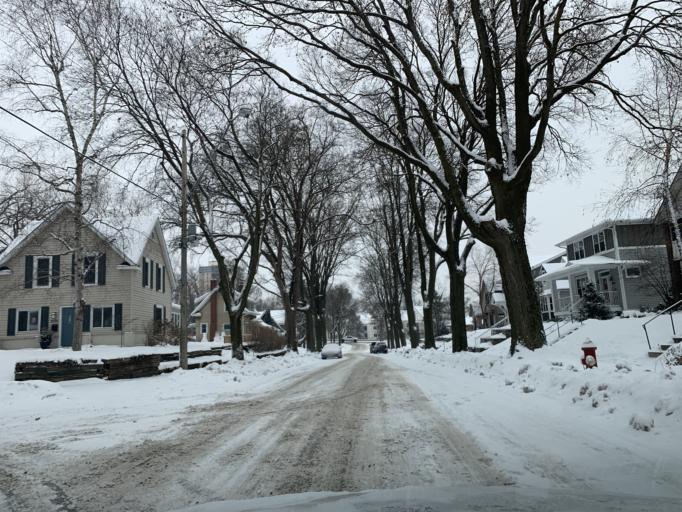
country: US
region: Minnesota
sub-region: Hennepin County
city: Saint Louis Park
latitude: 44.9500
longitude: -93.3250
